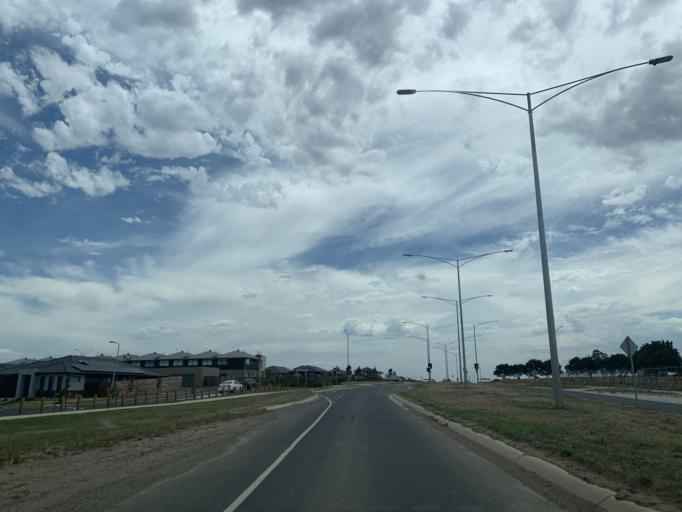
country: AU
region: Victoria
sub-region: Cardinia
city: Officer South
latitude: -38.1225
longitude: 145.3584
